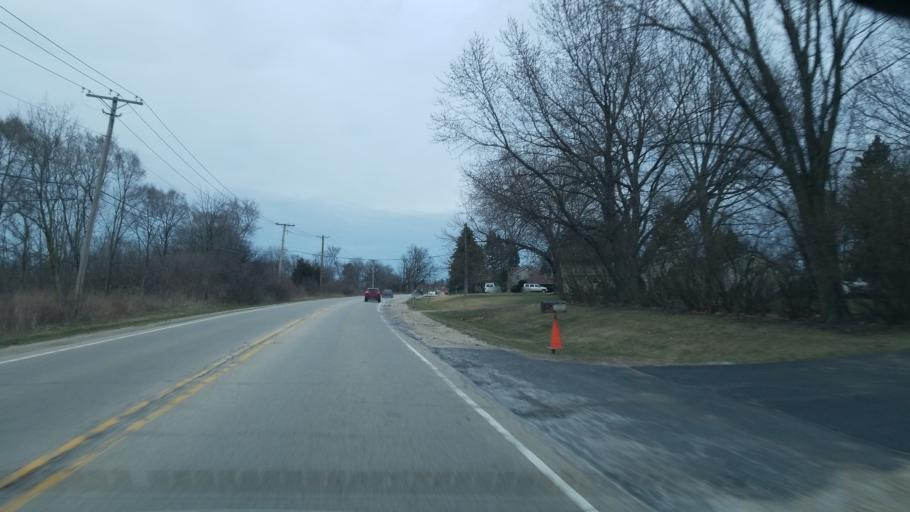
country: US
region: Illinois
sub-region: Kane County
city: Sleepy Hollow
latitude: 42.1012
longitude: -88.3100
